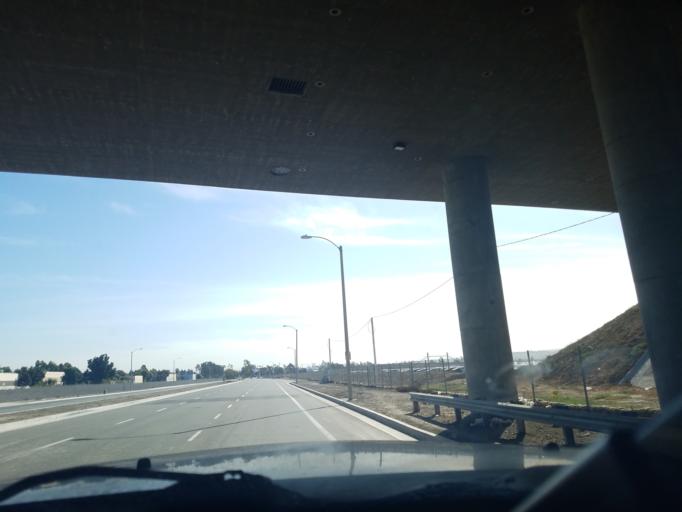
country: US
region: California
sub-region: Orange County
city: Tustin
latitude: 33.7132
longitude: -117.8141
